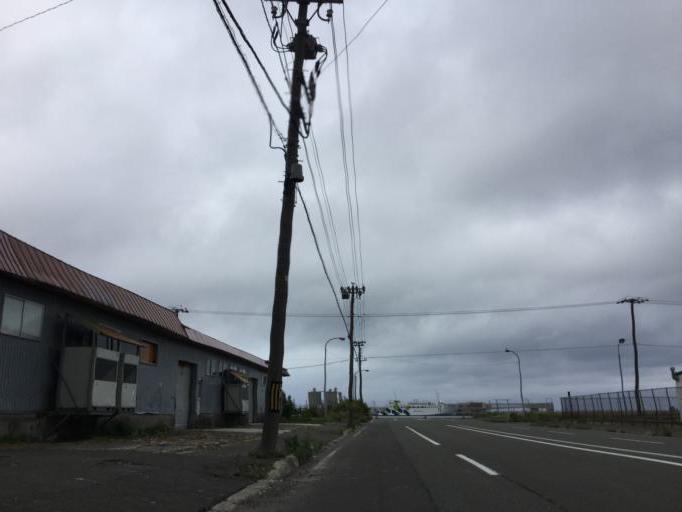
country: JP
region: Hokkaido
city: Wakkanai
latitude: 45.4087
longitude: 141.6822
